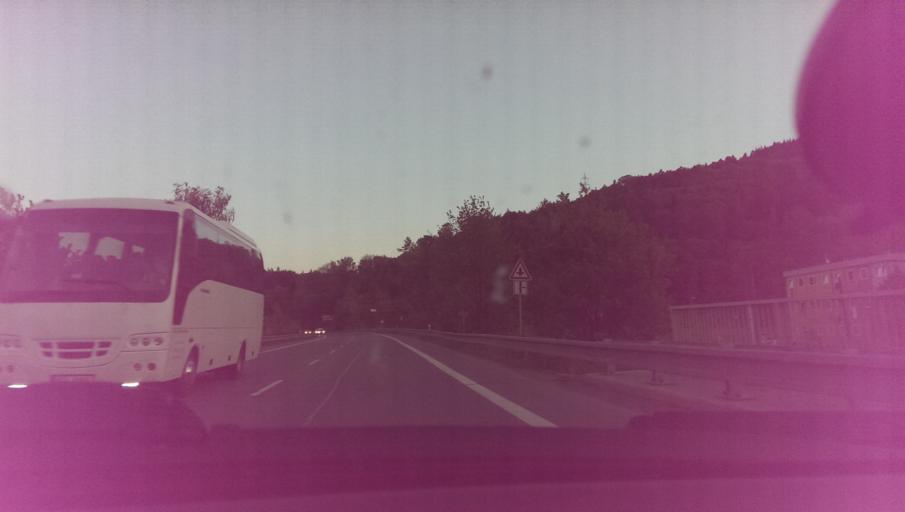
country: CZ
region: Zlin
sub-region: Okres Vsetin
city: Vsetin
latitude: 49.3490
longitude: 17.9706
